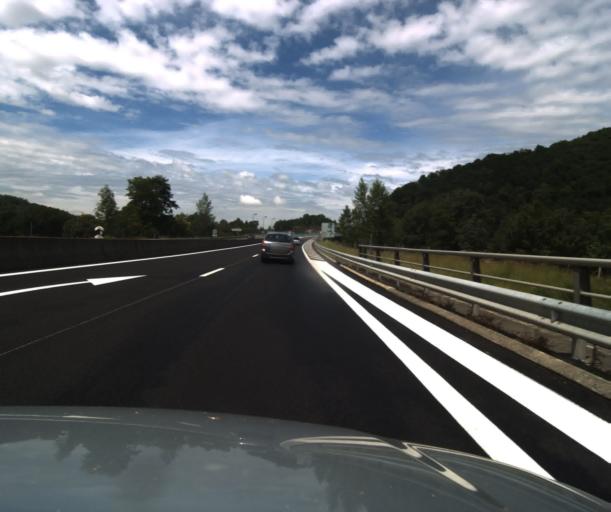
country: FR
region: Midi-Pyrenees
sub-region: Departement des Hautes-Pyrenees
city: Lourdes
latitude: 43.0794
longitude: -0.0445
